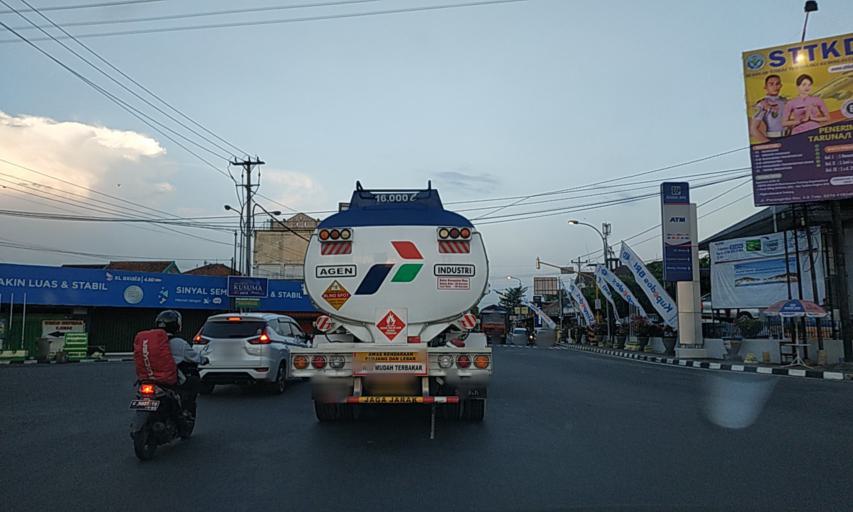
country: ID
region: Daerah Istimewa Yogyakarta
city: Srandakan
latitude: -7.8654
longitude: 110.1568
